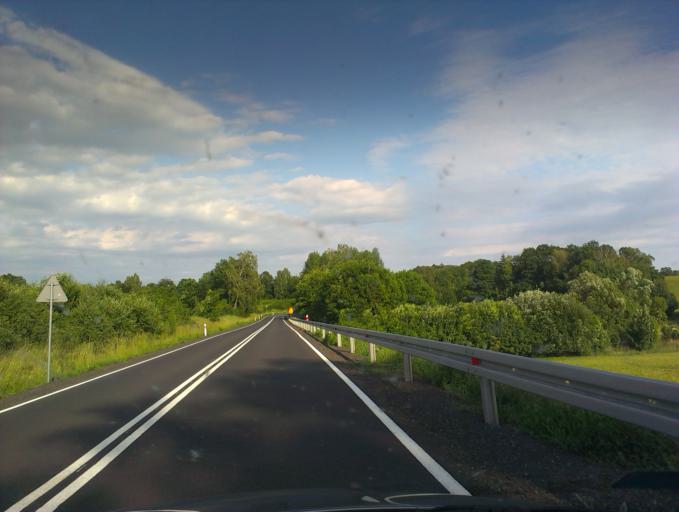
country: PL
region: West Pomeranian Voivodeship
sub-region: Powiat szczecinecki
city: Borne Sulinowo
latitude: 53.6192
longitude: 16.5362
